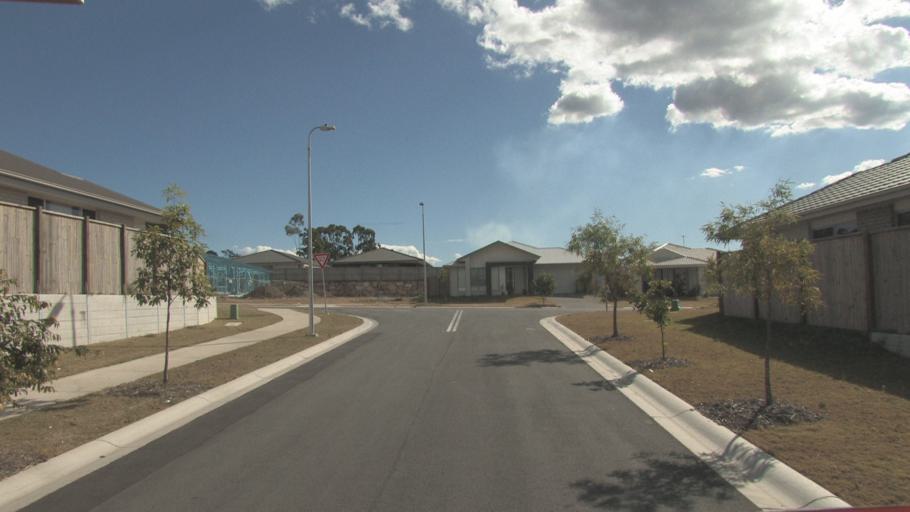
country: AU
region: Queensland
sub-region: Logan
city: Chambers Flat
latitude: -27.8040
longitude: 153.1199
